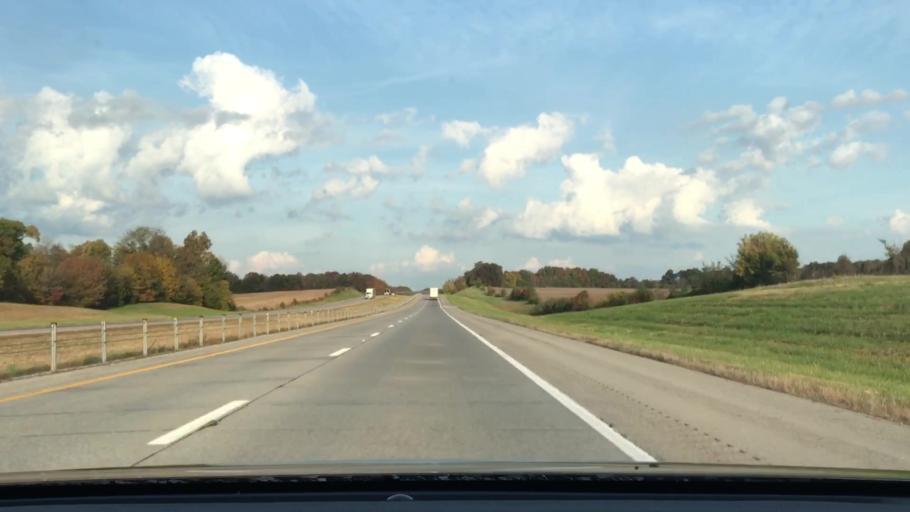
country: US
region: Kentucky
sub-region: Trigg County
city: Cadiz
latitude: 36.9207
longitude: -87.7978
